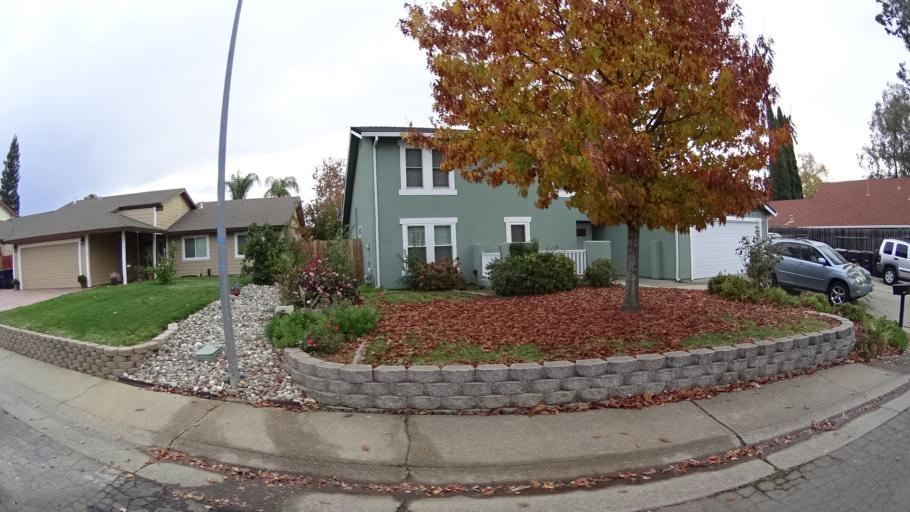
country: US
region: California
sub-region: Sacramento County
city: Citrus Heights
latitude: 38.7170
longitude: -121.2475
